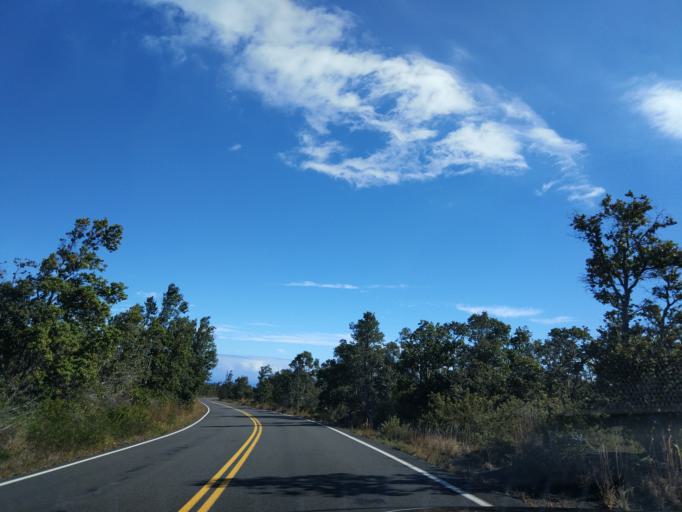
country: US
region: Hawaii
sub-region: Hawaii County
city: Volcano
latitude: 19.3421
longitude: -155.2113
